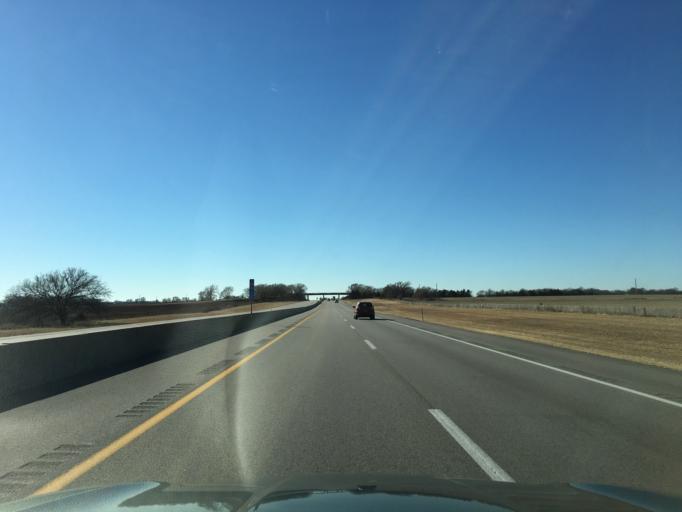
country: US
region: Kansas
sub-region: Sumner County
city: Belle Plaine
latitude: 37.3378
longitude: -97.3279
